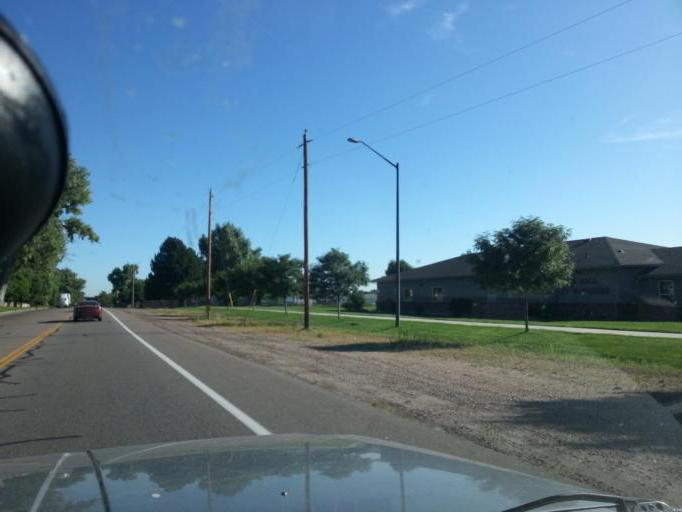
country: US
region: Colorado
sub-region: Larimer County
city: Fort Collins
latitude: 40.5095
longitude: -105.0392
